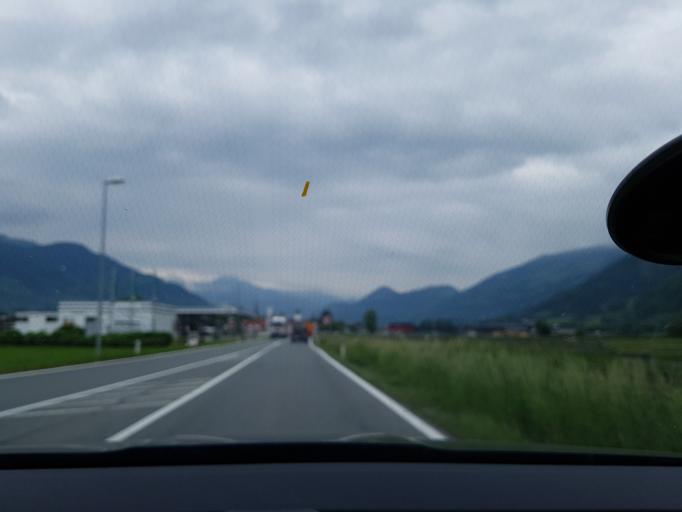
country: AT
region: Tyrol
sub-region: Politischer Bezirk Schwaz
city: Uderns
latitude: 47.3164
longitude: 11.8658
